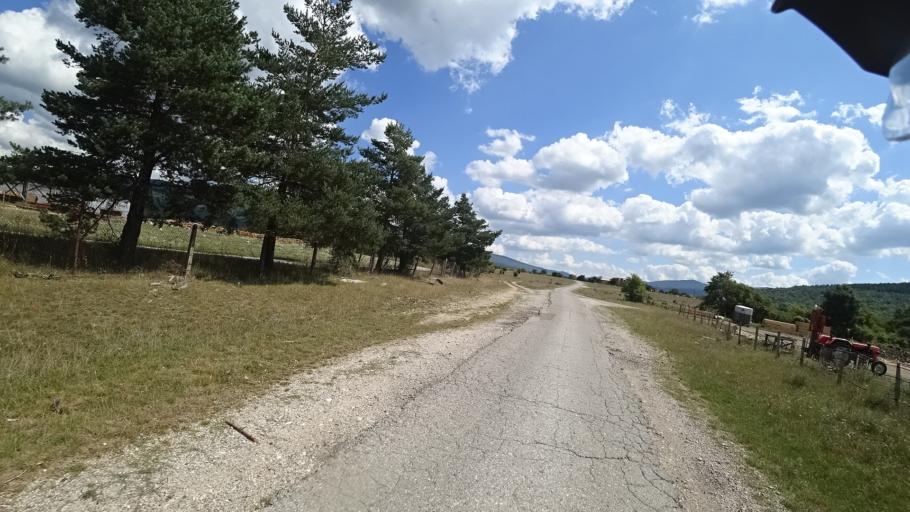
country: HR
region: Zadarska
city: Gracac
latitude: 44.5443
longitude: 15.7686
